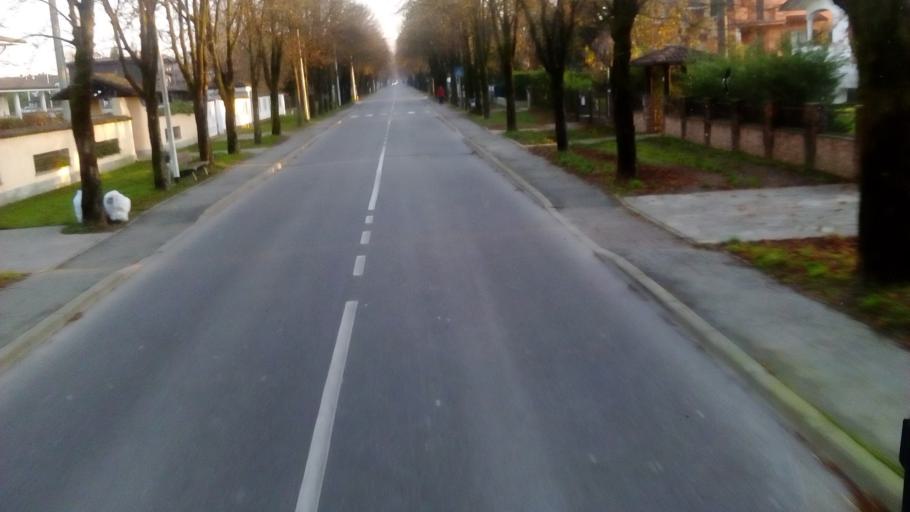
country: IT
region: Lombardy
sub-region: Provincia di Cremona
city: Castelleone
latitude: 45.3045
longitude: 9.7542
